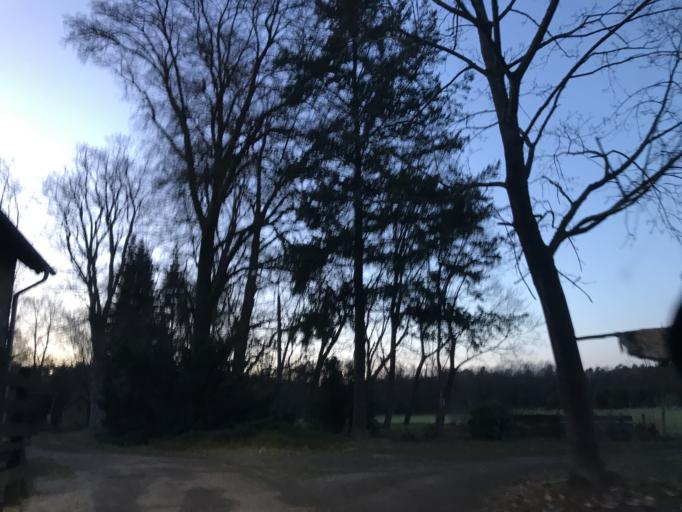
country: DE
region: Brandenburg
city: Nennhausen
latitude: 52.5337
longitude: 12.4796
